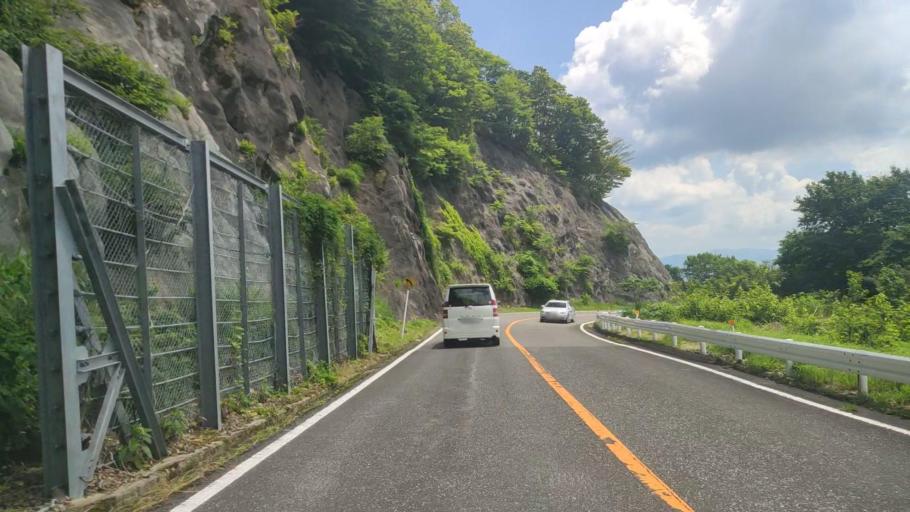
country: JP
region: Gifu
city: Tarui
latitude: 35.4015
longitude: 136.4266
